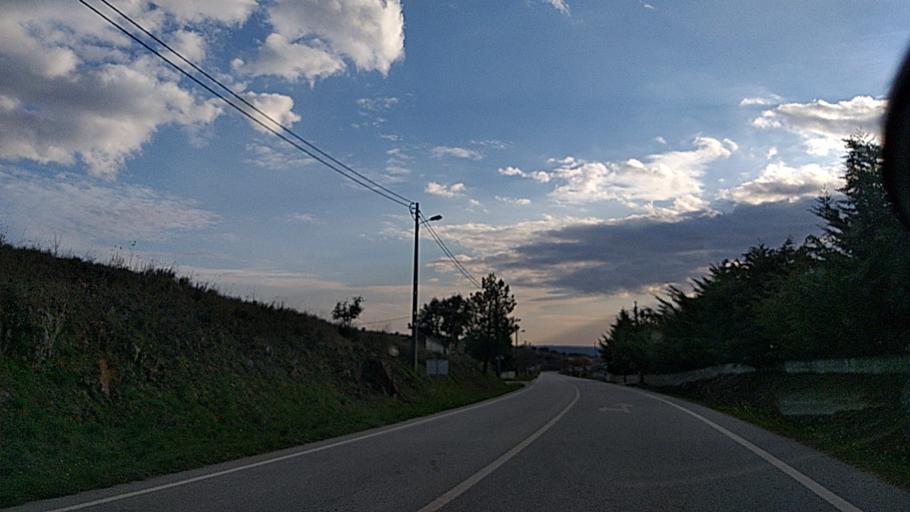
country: ES
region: Castille and Leon
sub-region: Provincia de Salamanca
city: Aldea del Obispo
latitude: 40.7187
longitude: -6.9054
